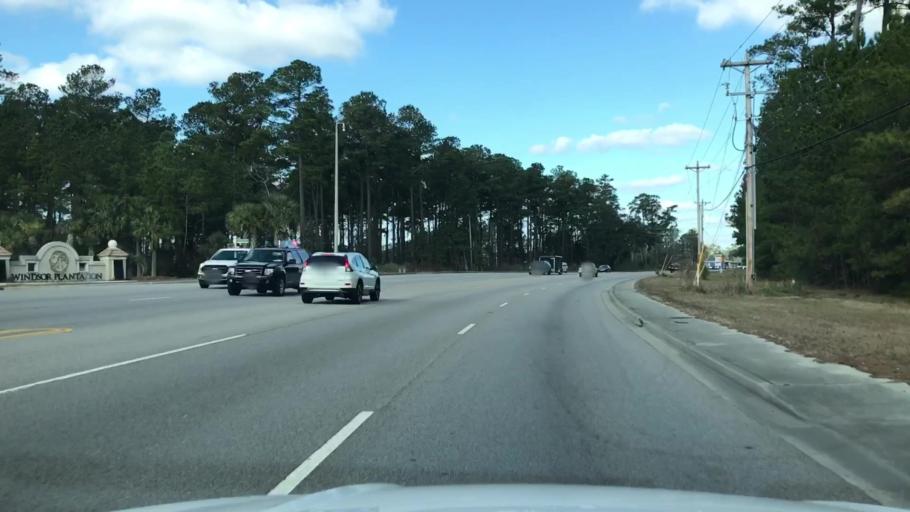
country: US
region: South Carolina
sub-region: Horry County
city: Socastee
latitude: 33.6564
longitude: -78.9916
